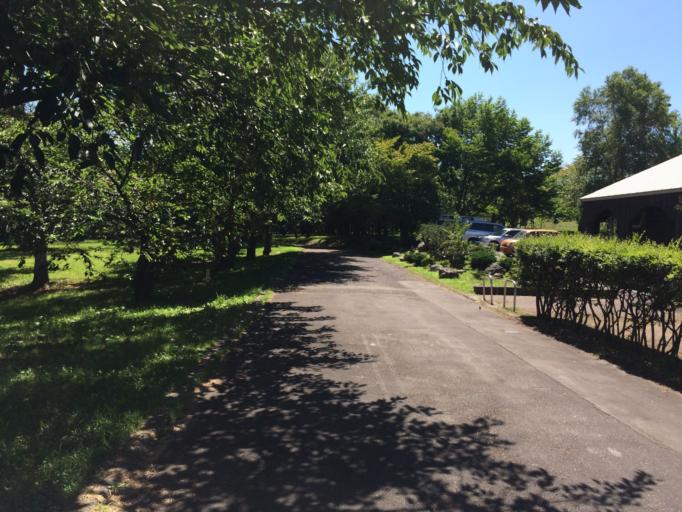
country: JP
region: Hokkaido
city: Nanae
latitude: 42.0993
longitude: 140.5682
